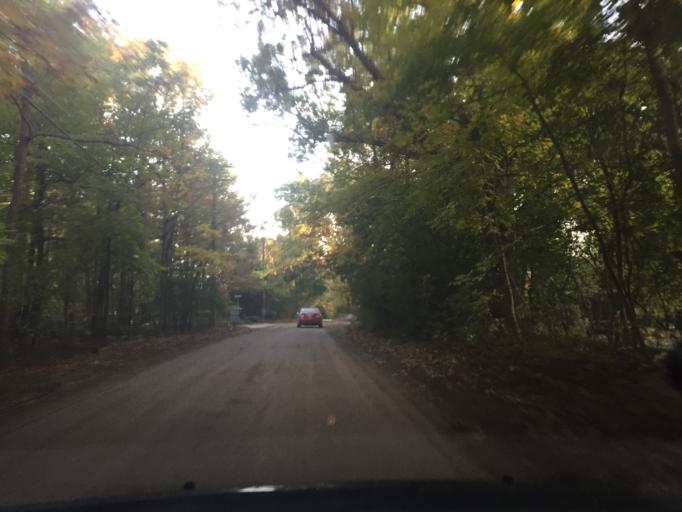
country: US
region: Michigan
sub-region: Oakland County
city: Bloomfield Hills
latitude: 42.5738
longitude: -83.2921
